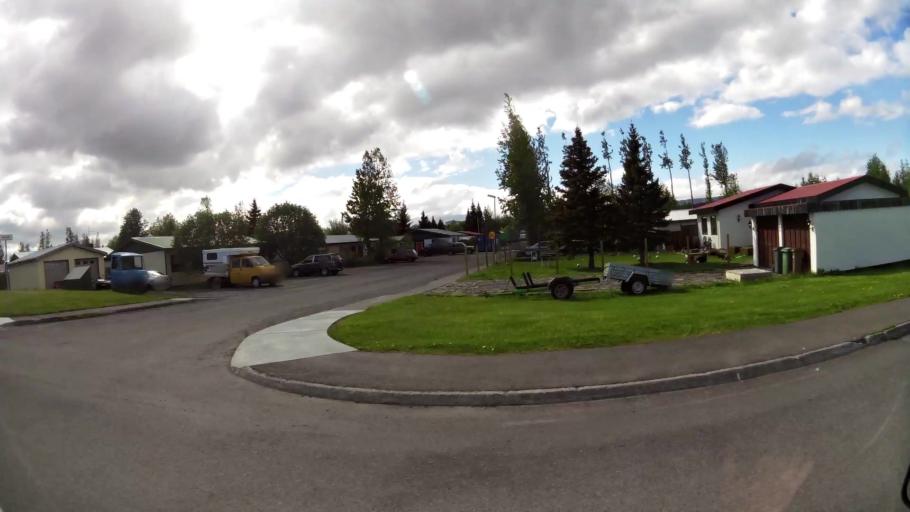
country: IS
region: East
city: Egilsstadir
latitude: 65.2690
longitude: -14.3856
